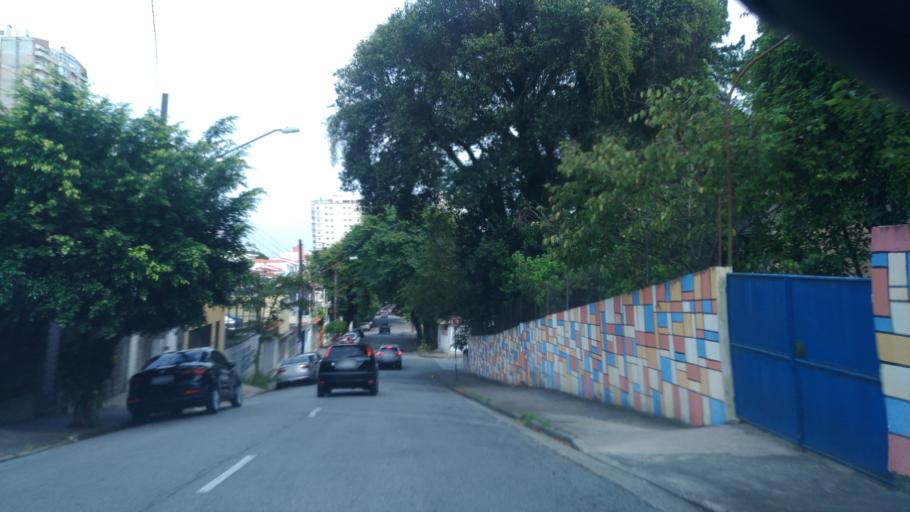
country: BR
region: Sao Paulo
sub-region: Sao Bernardo Do Campo
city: Sao Bernardo do Campo
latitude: -23.7083
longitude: -46.5419
